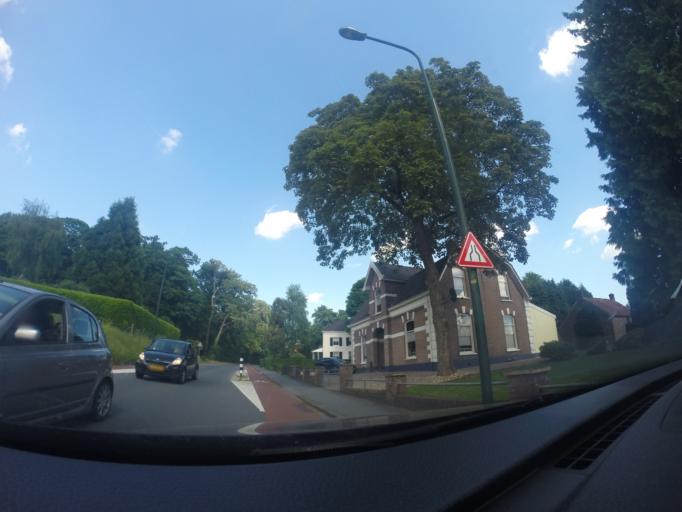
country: NL
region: Gelderland
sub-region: Gemeente Renkum
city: Oosterbeek
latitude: 51.9778
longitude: 5.8281
